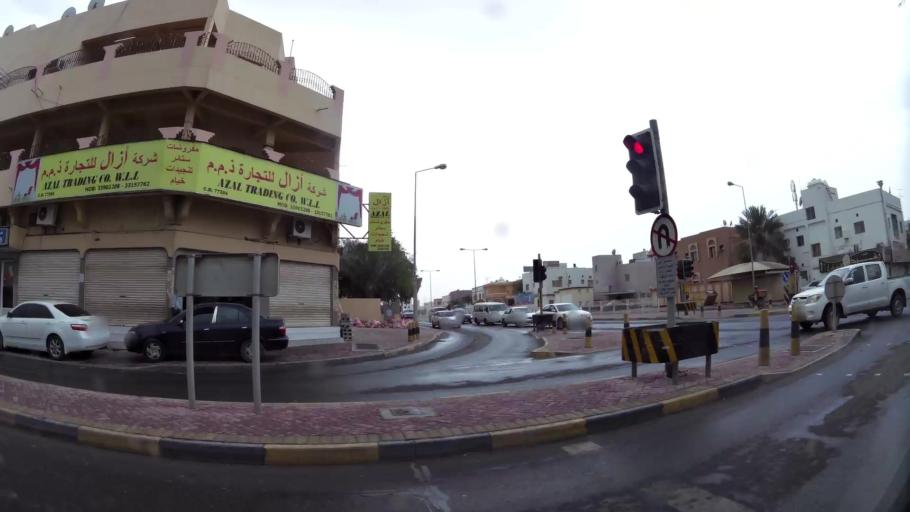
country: BH
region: Northern
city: Ar Rifa'
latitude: 26.1300
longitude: 50.5655
